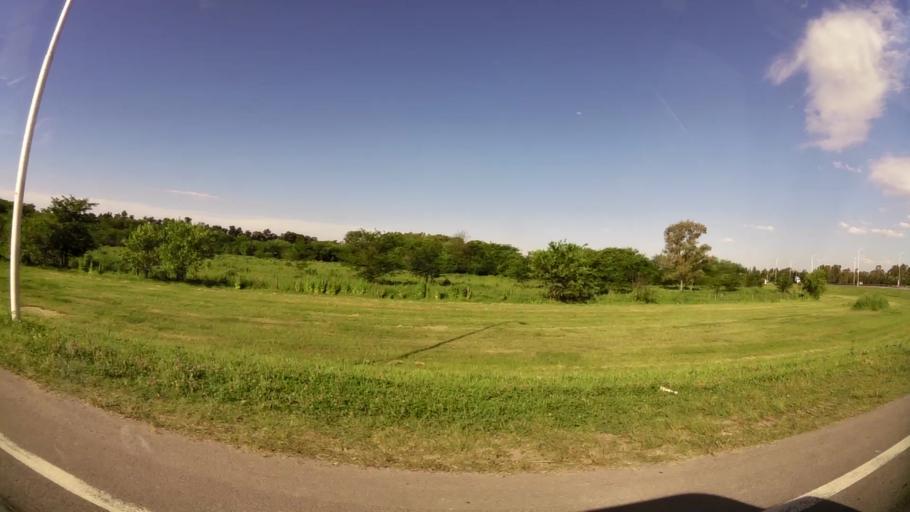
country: AR
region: Buenos Aires
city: Hurlingham
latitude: -34.5659
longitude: -58.6400
